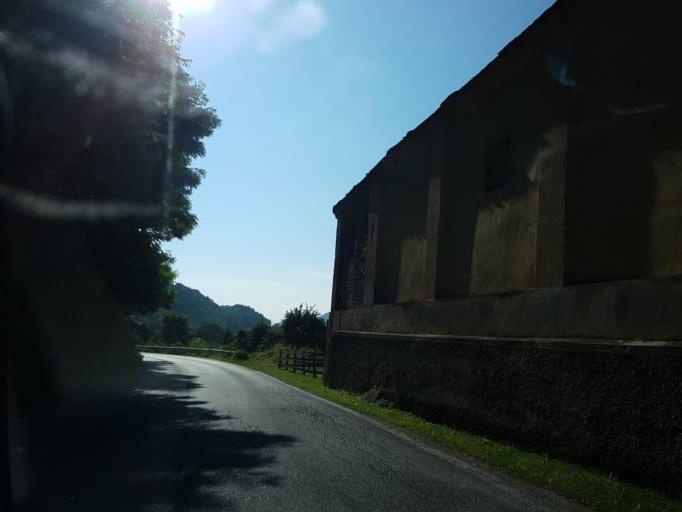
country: IT
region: Piedmont
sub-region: Provincia di Cuneo
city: San Damiano Macra
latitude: 44.4873
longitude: 7.2661
